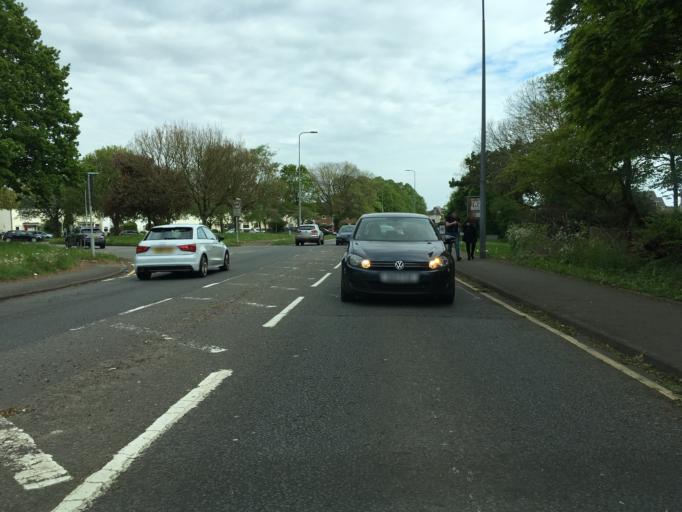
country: GB
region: Wales
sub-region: Caerphilly County Borough
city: Caerphilly
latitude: 51.5305
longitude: -3.2036
